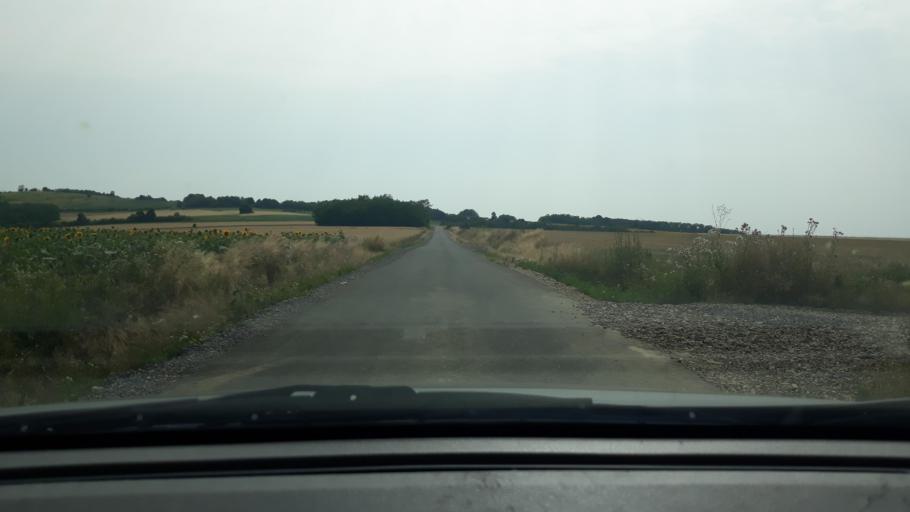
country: RO
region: Bihor
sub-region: Comuna Tauteu
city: Tauteu
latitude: 47.2642
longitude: 22.3021
